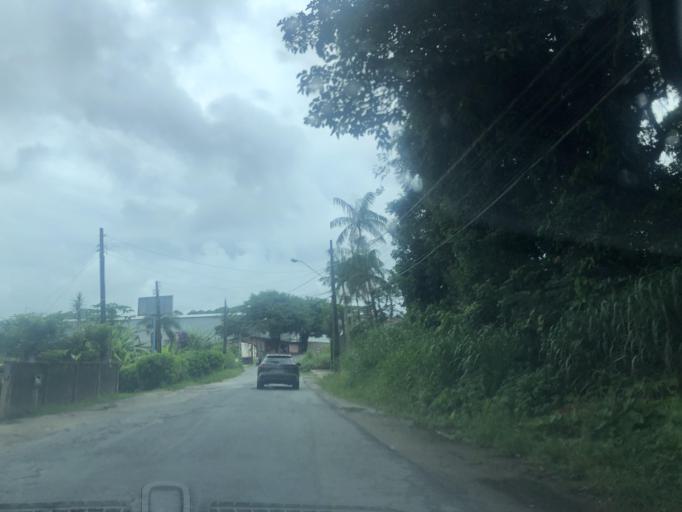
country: BR
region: Santa Catarina
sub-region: Sao Francisco Do Sul
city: Sao Francisco do Sul
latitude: -26.2389
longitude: -48.6159
